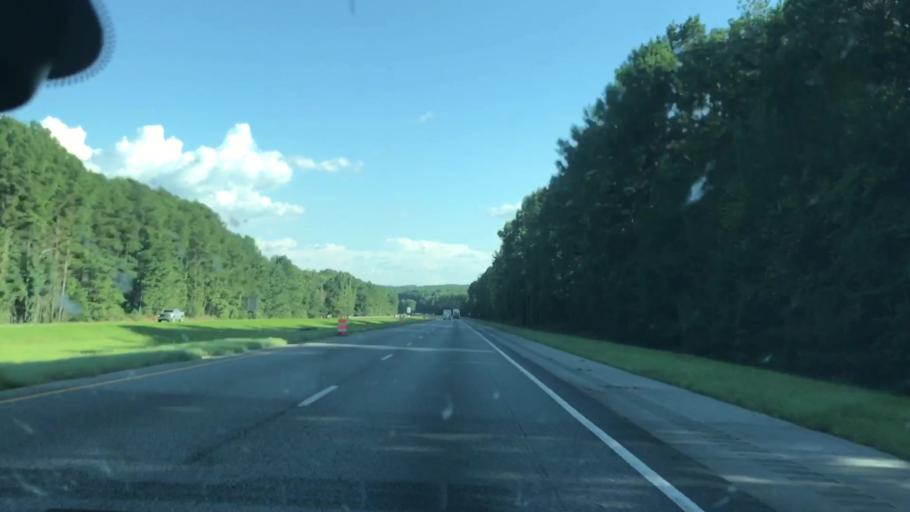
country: US
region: Georgia
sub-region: Harris County
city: Hamilton
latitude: 32.6469
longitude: -84.9717
